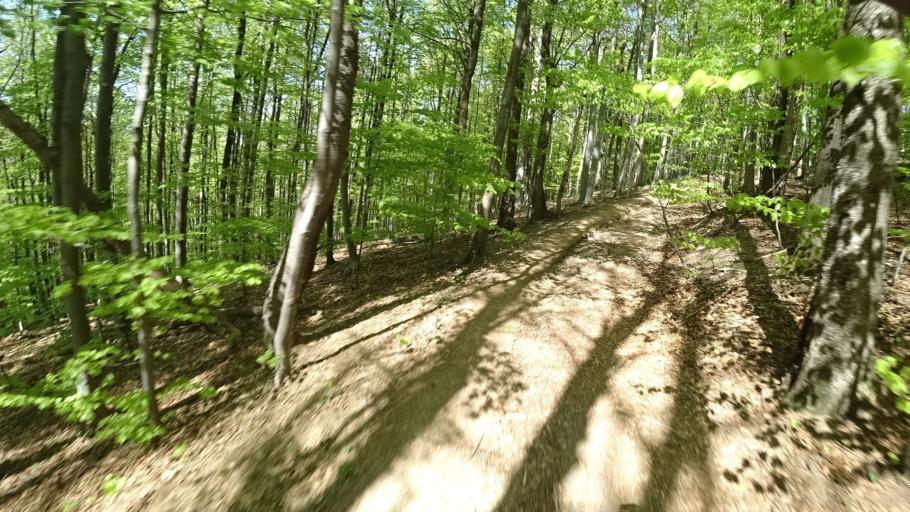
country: HR
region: Zagrebacka
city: Jablanovec
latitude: 45.8799
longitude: 15.9071
